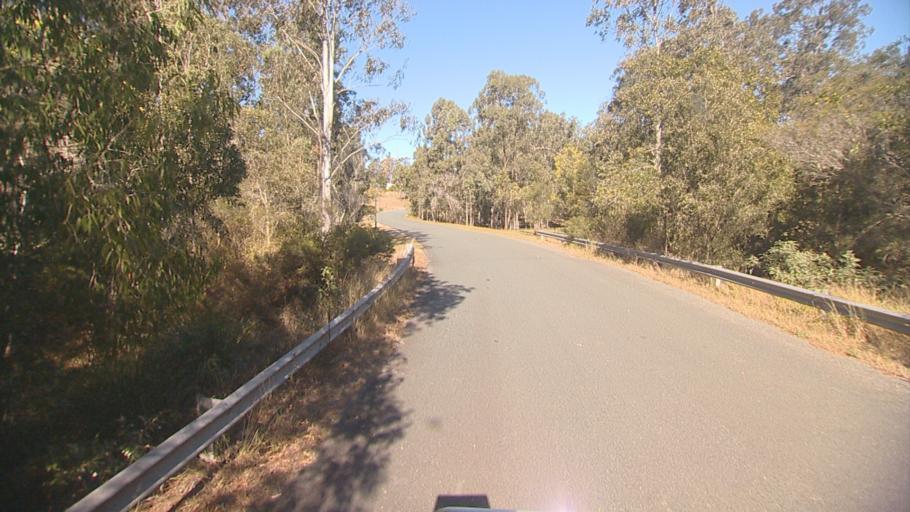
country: AU
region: Queensland
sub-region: Ipswich
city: Springfield Lakes
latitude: -27.7146
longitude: 152.9311
